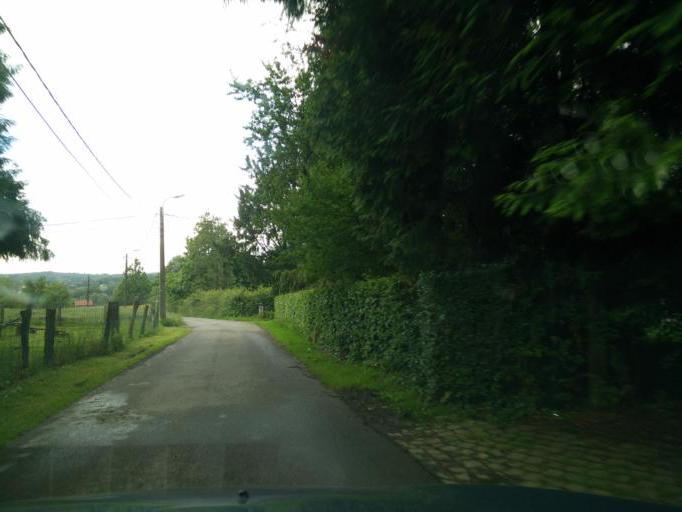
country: BE
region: Wallonia
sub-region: Province du Brabant Wallon
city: Braine-le-Chateau
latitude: 50.7139
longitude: 4.3083
